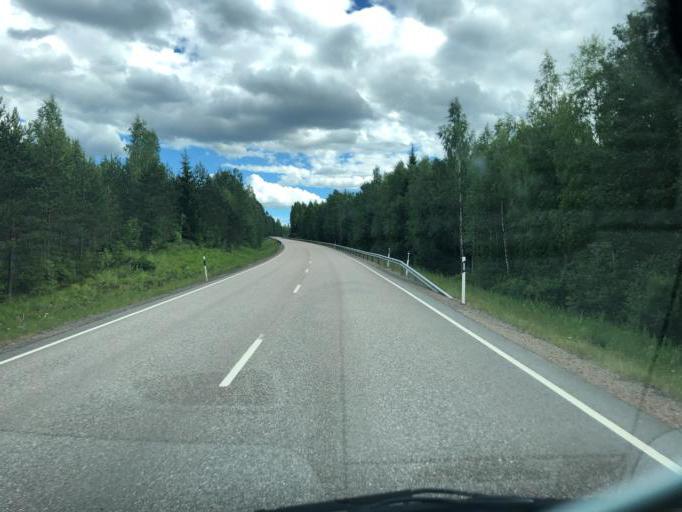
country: FI
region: Southern Savonia
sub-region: Mikkeli
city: Maentyharju
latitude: 61.1147
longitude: 27.0986
